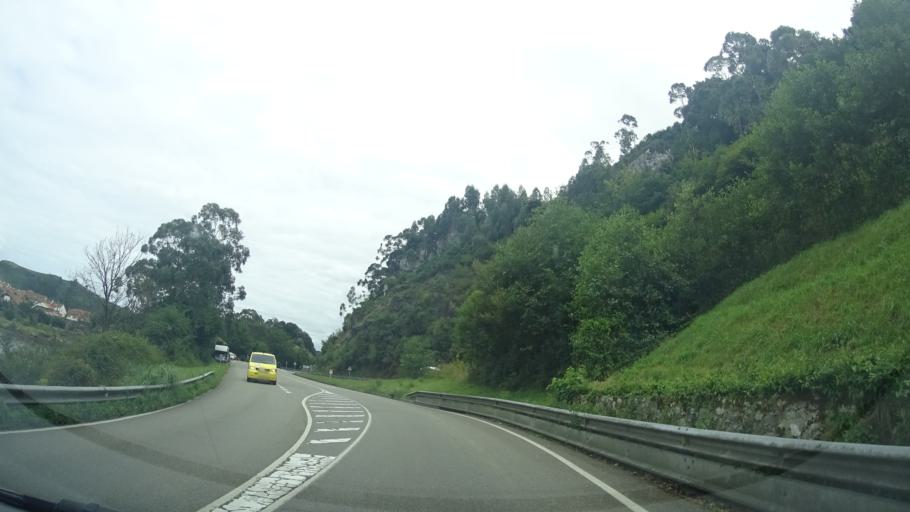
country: ES
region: Asturias
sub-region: Province of Asturias
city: Ribadesella
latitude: 43.4636
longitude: -5.0740
